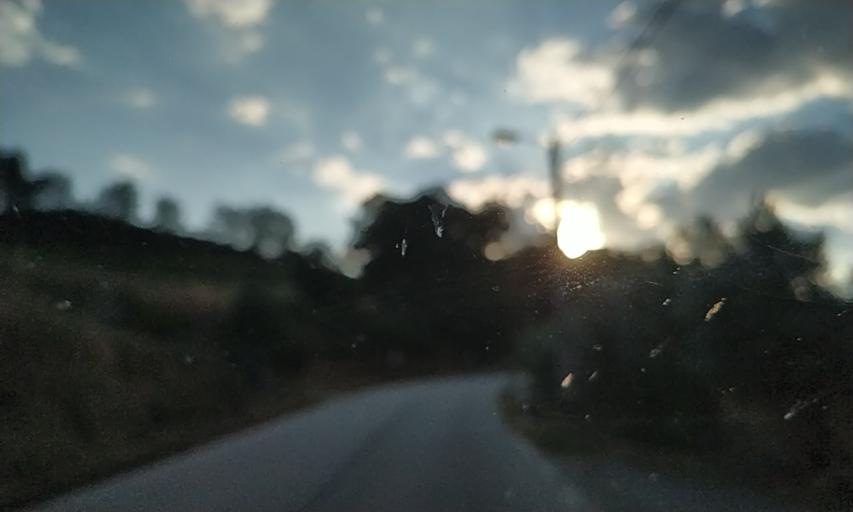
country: PT
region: Viseu
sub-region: Sao Joao da Pesqueira
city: Sao Joao da Pesqueira
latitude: 41.2530
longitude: -7.4368
